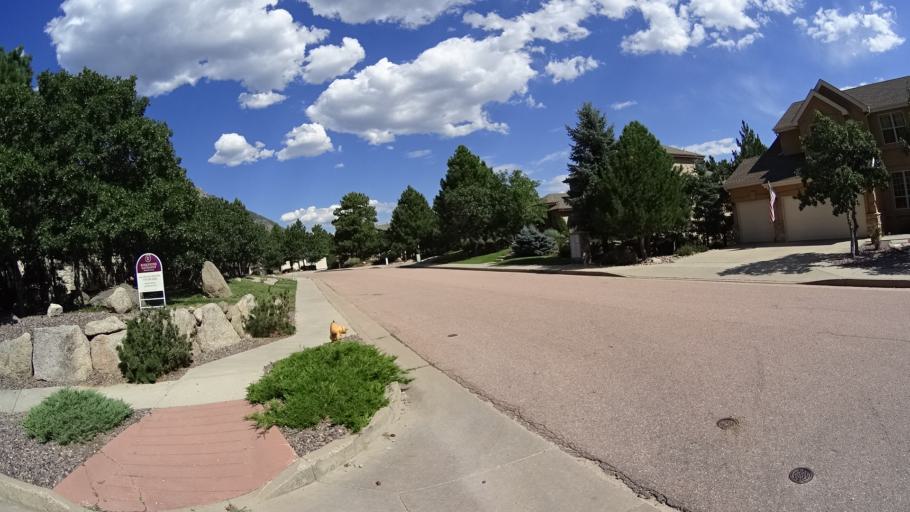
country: US
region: Colorado
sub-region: El Paso County
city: Fort Carson
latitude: 38.7429
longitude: -104.8340
